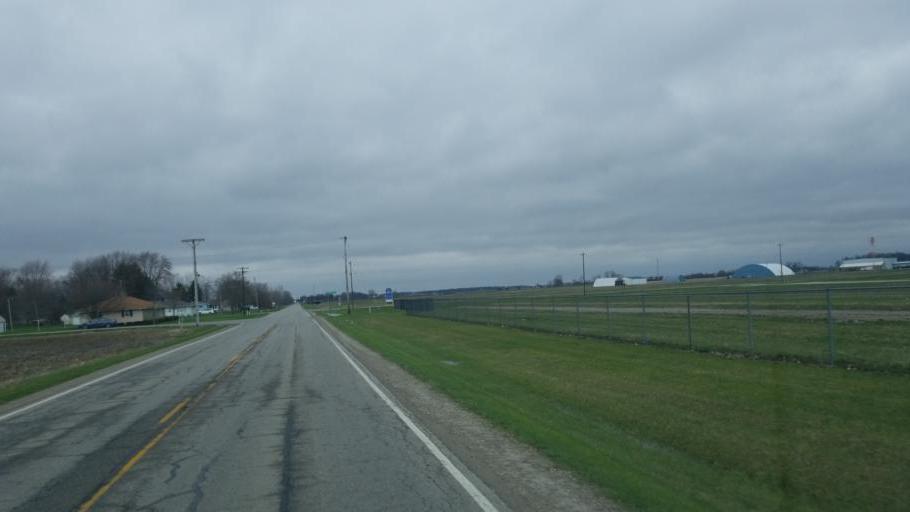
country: US
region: Ohio
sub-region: Marion County
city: Marion
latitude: 40.6140
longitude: -83.0733
